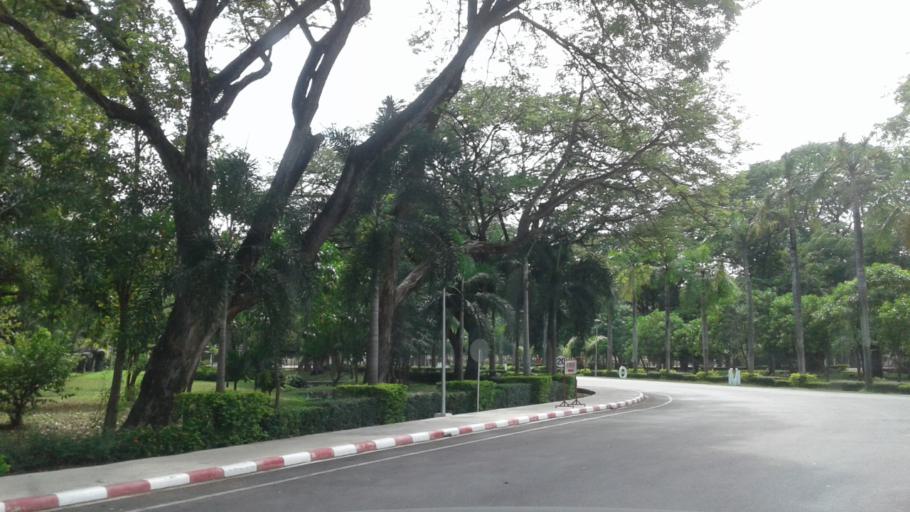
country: TH
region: Pathum Thani
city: Khlong Luang
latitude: 14.0782
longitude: 100.6141
